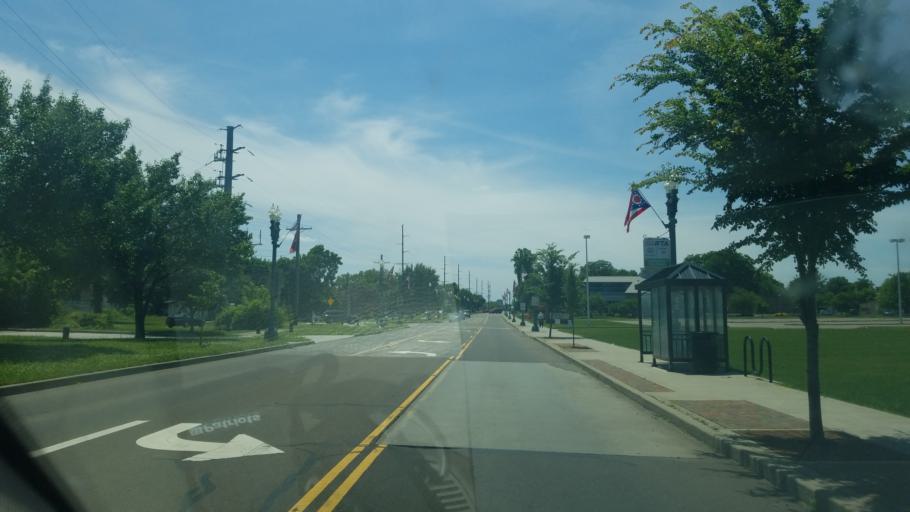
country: US
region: Ohio
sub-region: Stark County
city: Canton
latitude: 40.8160
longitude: -81.3328
